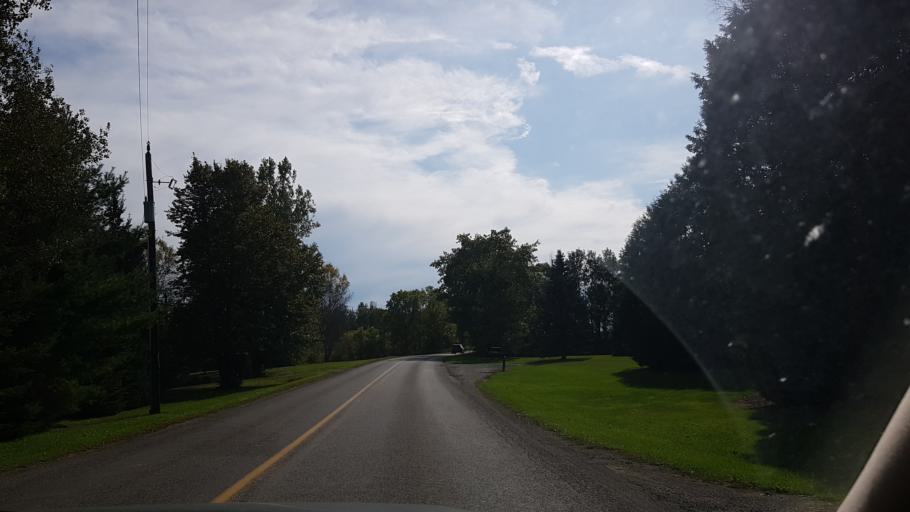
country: CA
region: Ontario
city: Delaware
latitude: 42.9115
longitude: -81.4704
